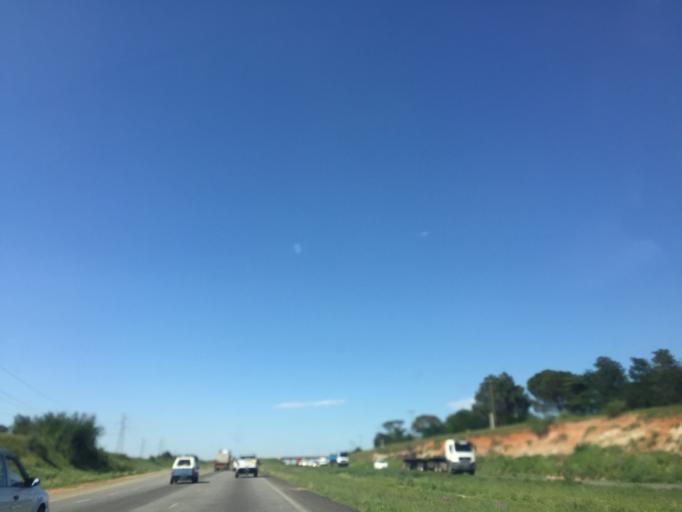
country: ZA
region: Gauteng
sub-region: Sedibeng District Municipality
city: Vereeniging
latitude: -26.6216
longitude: 27.9697
